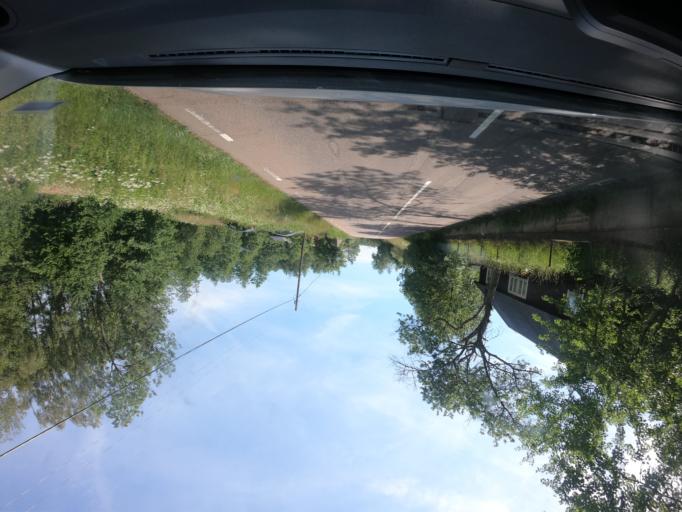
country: SE
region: Skane
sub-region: Bastads Kommun
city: Bastad
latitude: 56.4010
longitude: 12.9419
